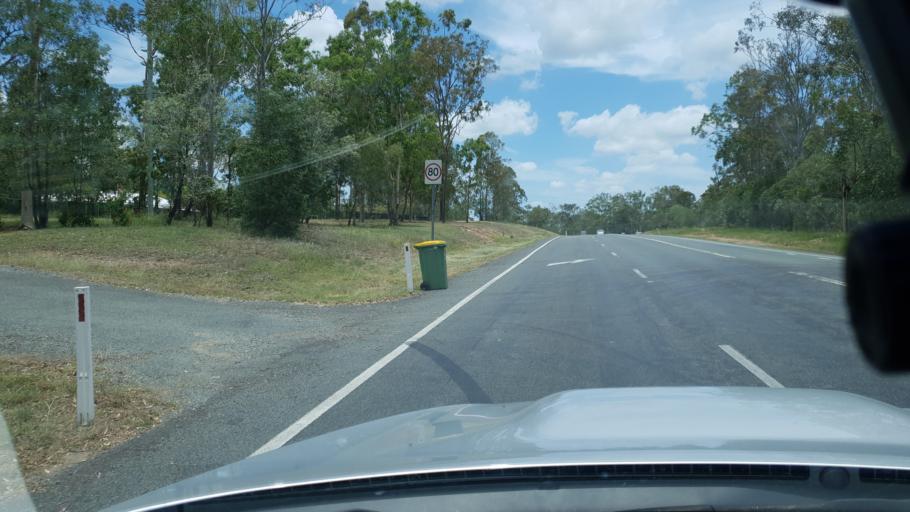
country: AU
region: Queensland
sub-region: Logan
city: North Maclean
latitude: -27.7713
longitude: 152.9822
